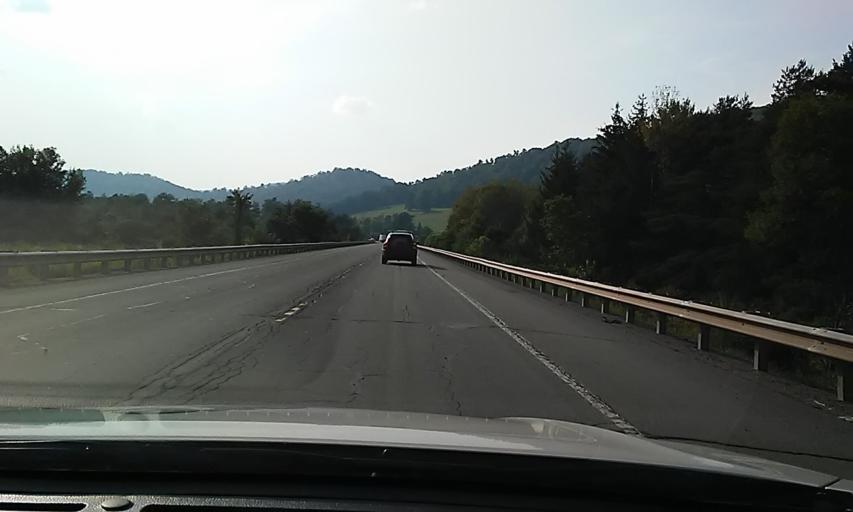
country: US
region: Pennsylvania
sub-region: McKean County
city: Port Allegany
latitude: 41.7875
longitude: -78.1694
